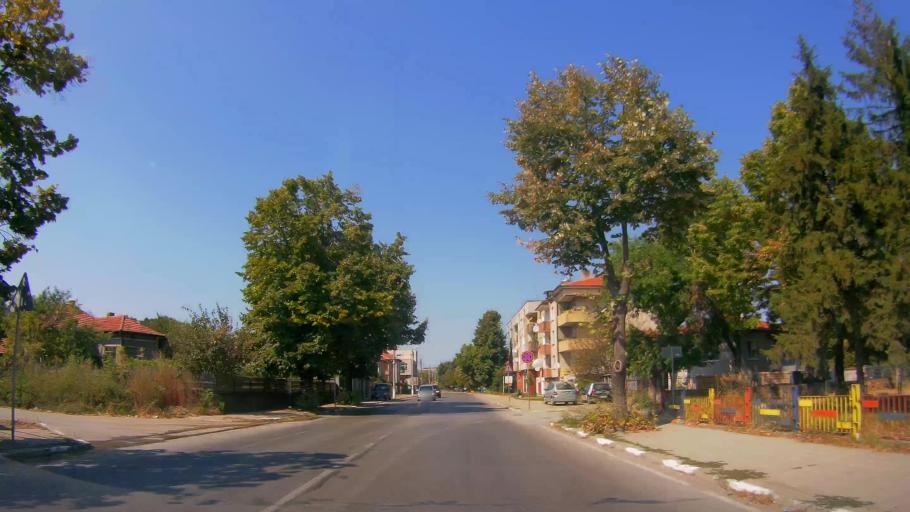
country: BG
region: Razgrad
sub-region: Obshtina Tsar Kaloyan
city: Tsar Kaloyan
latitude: 43.6071
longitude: 26.2390
